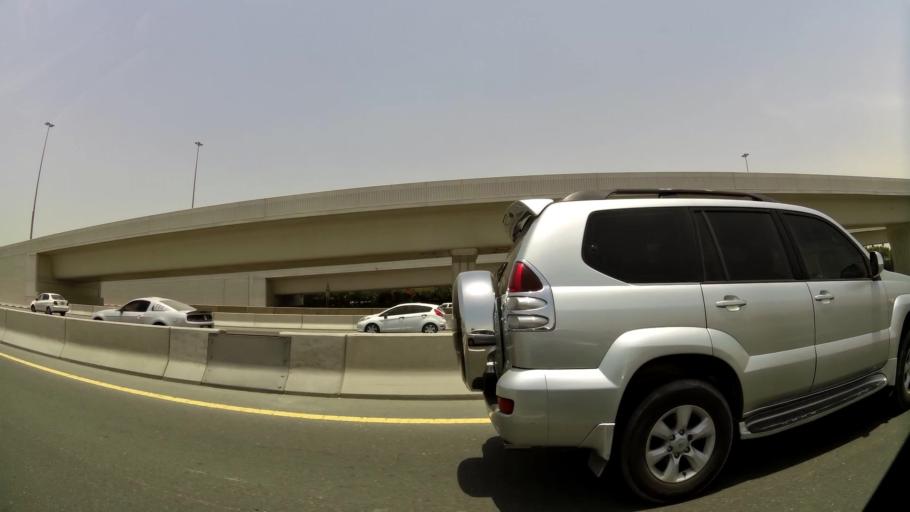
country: AE
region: Ash Shariqah
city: Sharjah
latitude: 25.2249
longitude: 55.3609
